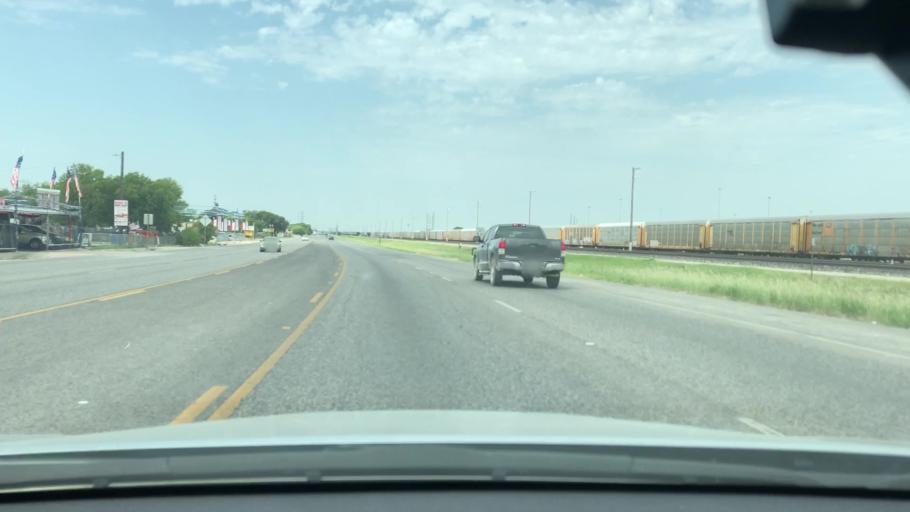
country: US
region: Texas
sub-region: Bexar County
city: Kirby
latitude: 29.4737
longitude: -98.3833
